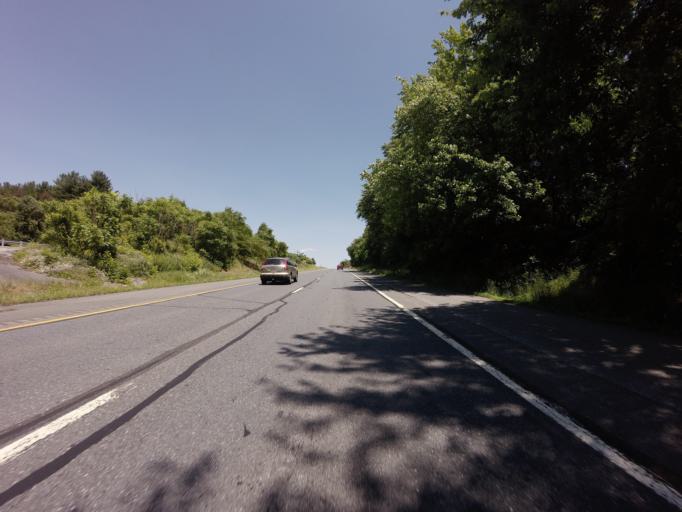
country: US
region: Maryland
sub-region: Frederick County
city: Brunswick
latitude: 39.3306
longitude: -77.6662
